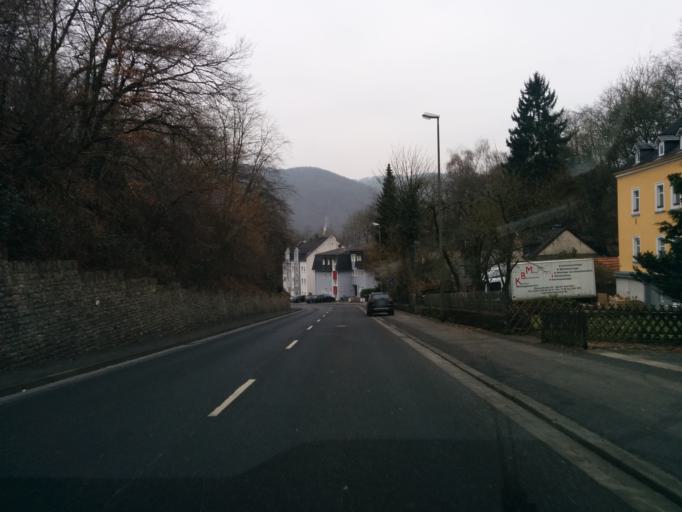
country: DE
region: Rheinland-Pfalz
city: Bad Ems
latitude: 50.3387
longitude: 7.7061
